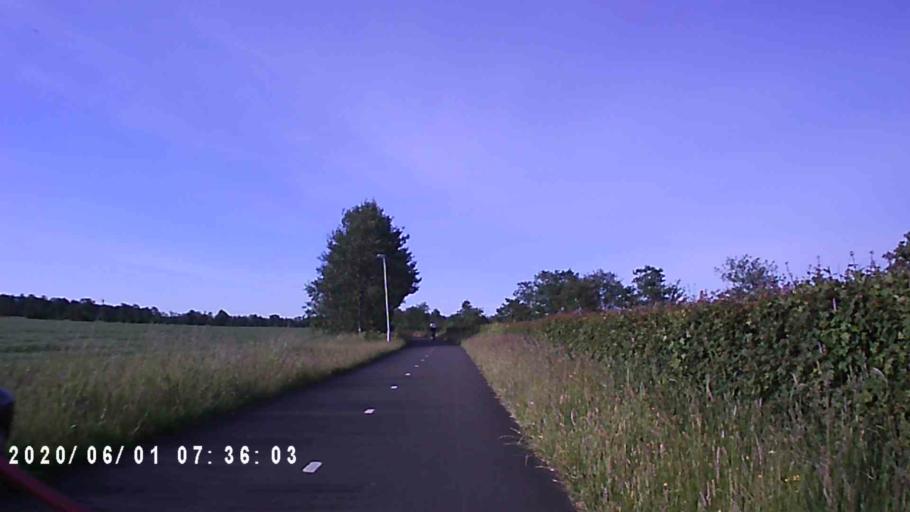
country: NL
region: Friesland
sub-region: Gemeente Dantumadiel
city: Damwald
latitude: 53.3044
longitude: 5.9944
